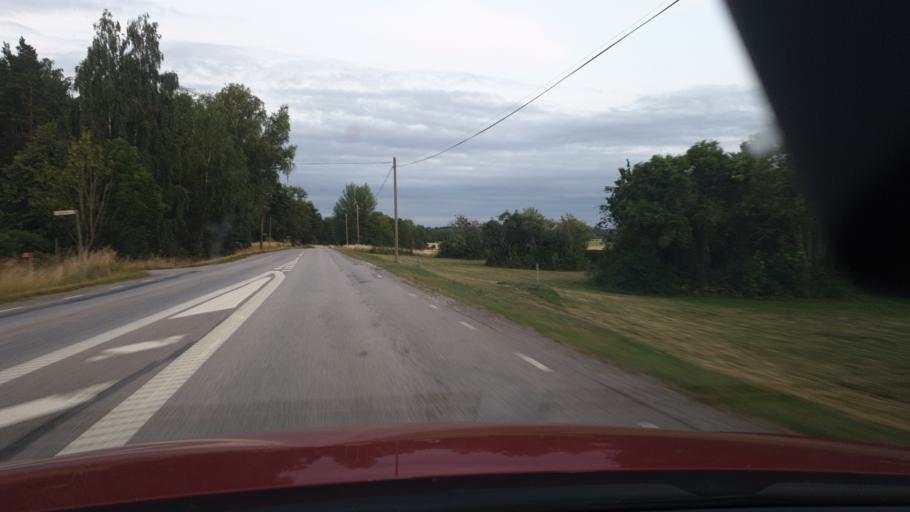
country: SE
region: Uppsala
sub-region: Habo Kommun
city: Balsta
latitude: 59.6017
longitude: 17.5073
